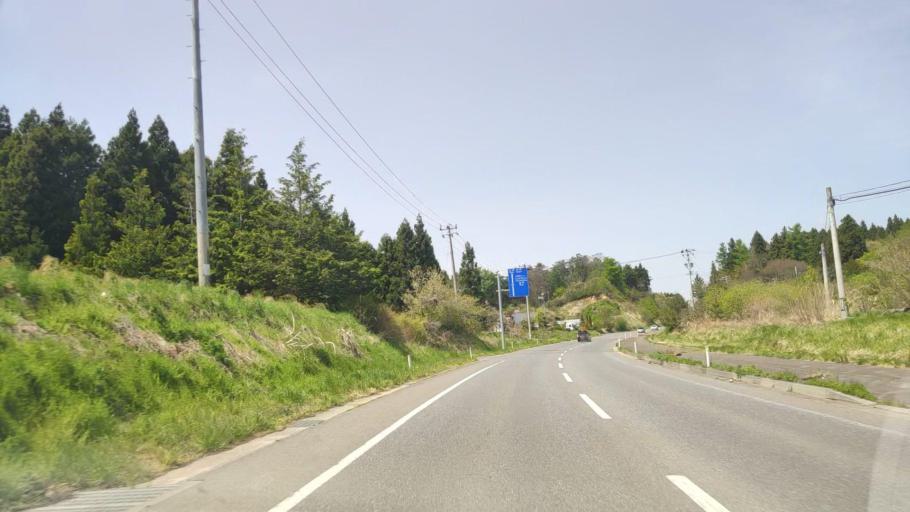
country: JP
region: Aomori
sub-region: Hachinohe Shi
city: Uchimaru
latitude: 40.5220
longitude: 141.4174
